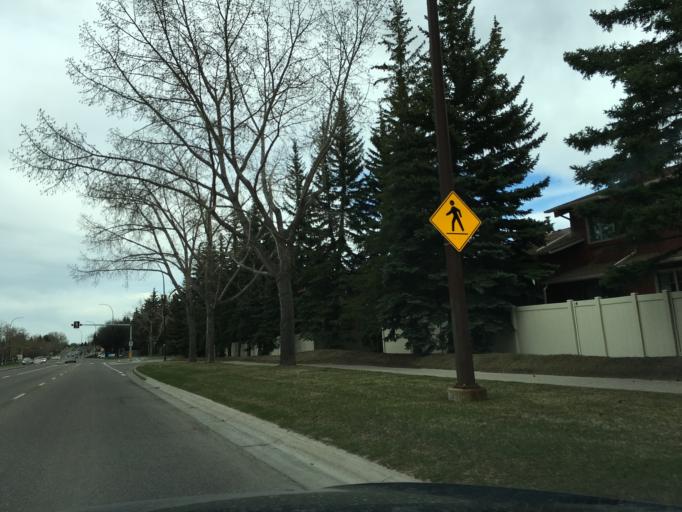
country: CA
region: Alberta
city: Calgary
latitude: 50.9613
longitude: -114.1113
